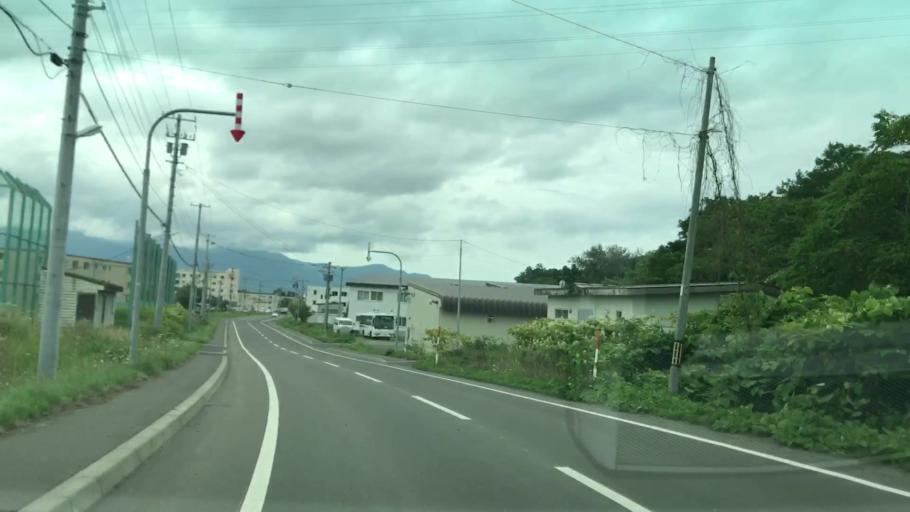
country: JP
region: Hokkaido
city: Iwanai
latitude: 43.0370
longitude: 140.5419
